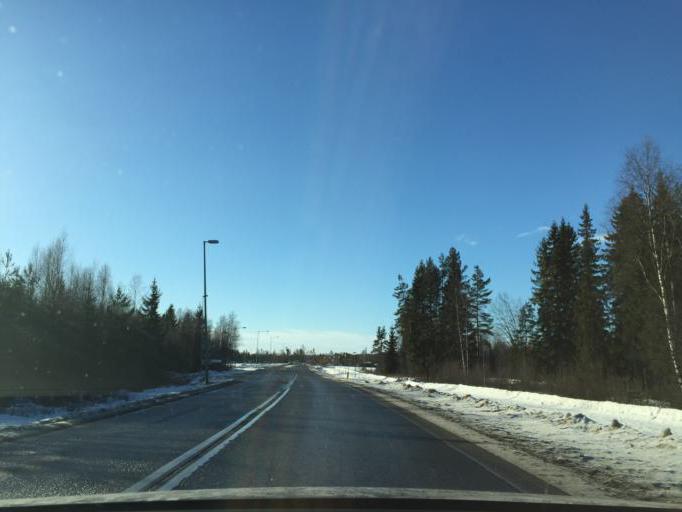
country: NO
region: Akershus
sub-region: Nes
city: Arnes
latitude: 60.1850
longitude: 11.5329
